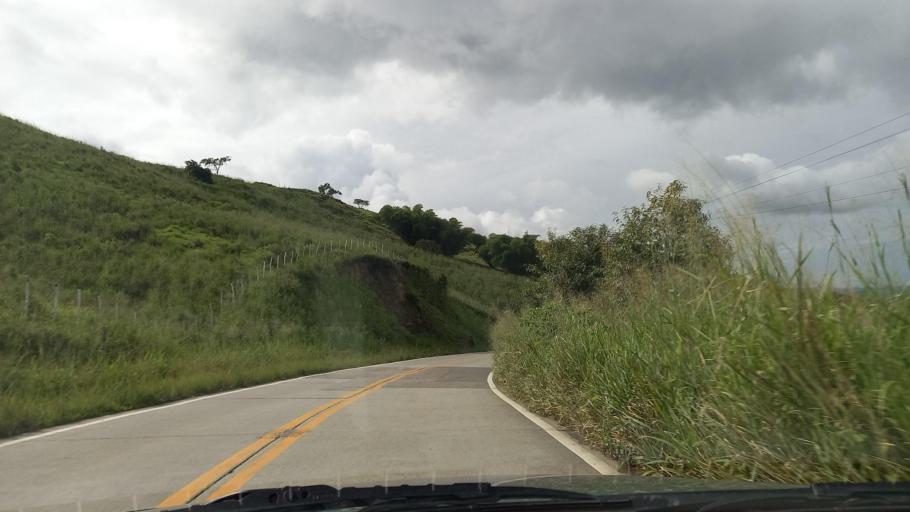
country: BR
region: Pernambuco
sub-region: Maraial
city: Maraial
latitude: -8.7856
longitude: -35.8776
